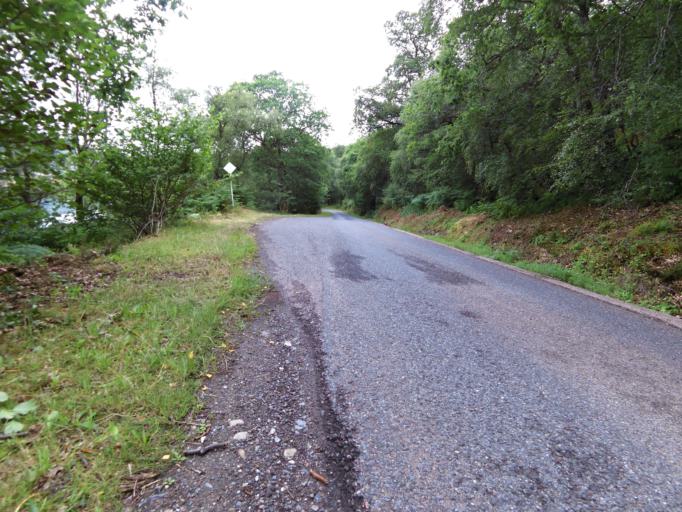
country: GB
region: Scotland
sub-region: Highland
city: Fort William
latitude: 56.8306
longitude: -5.1251
